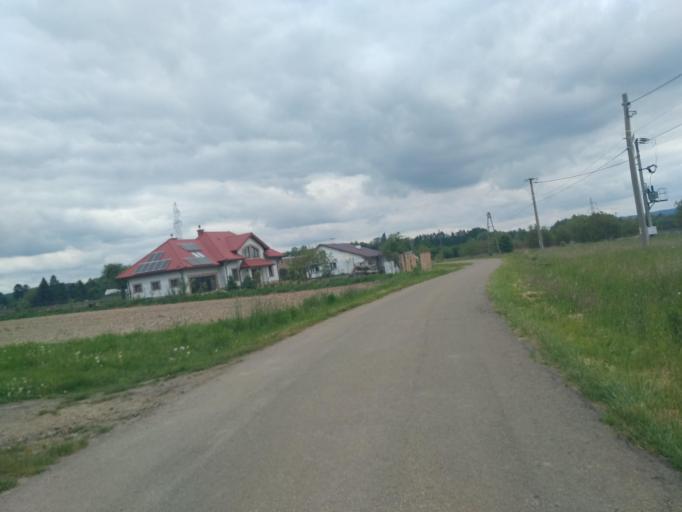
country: PL
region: Subcarpathian Voivodeship
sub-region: Powiat krosnienski
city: Jedlicze
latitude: 49.7127
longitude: 21.6871
